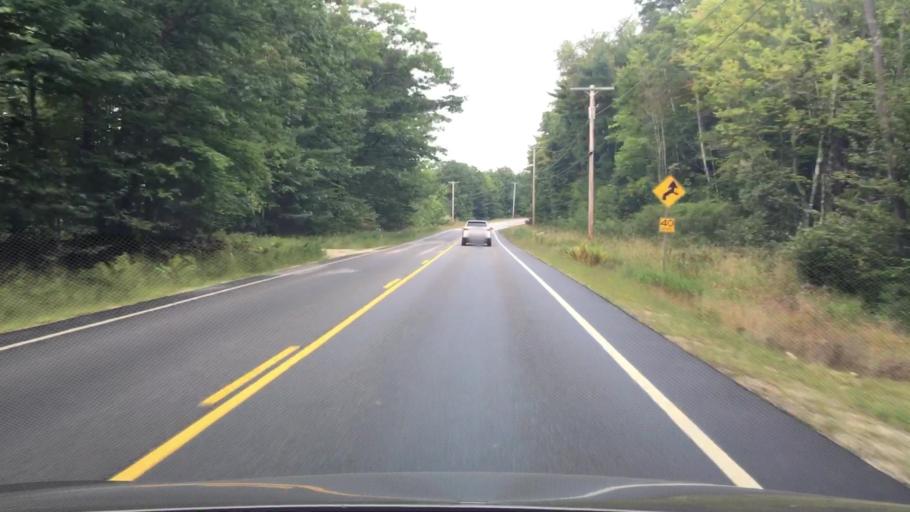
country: US
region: Maine
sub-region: Oxford County
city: Hartford
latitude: 44.3626
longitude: -70.3137
